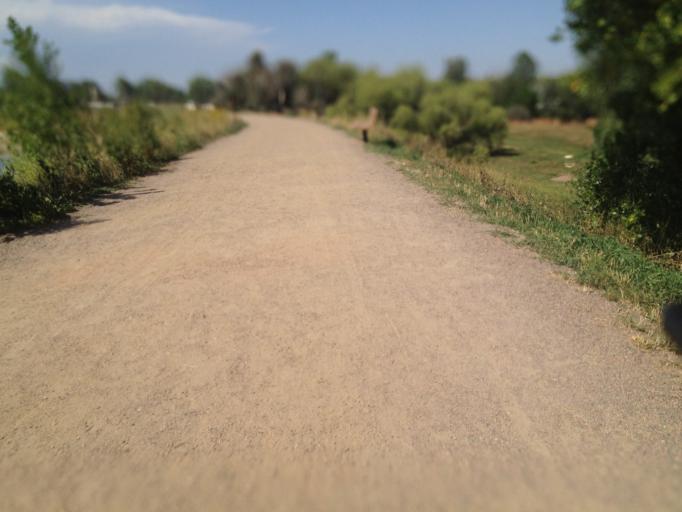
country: US
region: Colorado
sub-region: Boulder County
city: Lafayette
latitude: 39.9960
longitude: -105.1092
